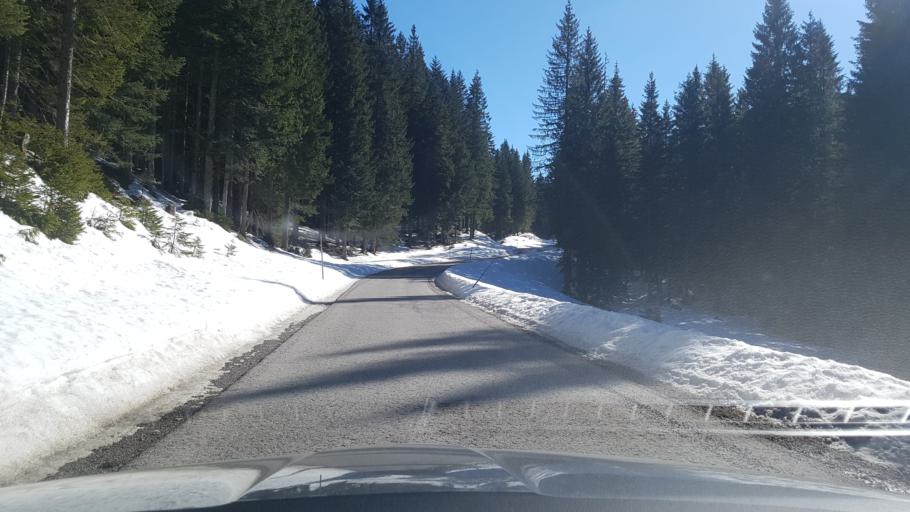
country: AT
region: Salzburg
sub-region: Politischer Bezirk Hallein
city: Abtenau
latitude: 47.6316
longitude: 13.4135
